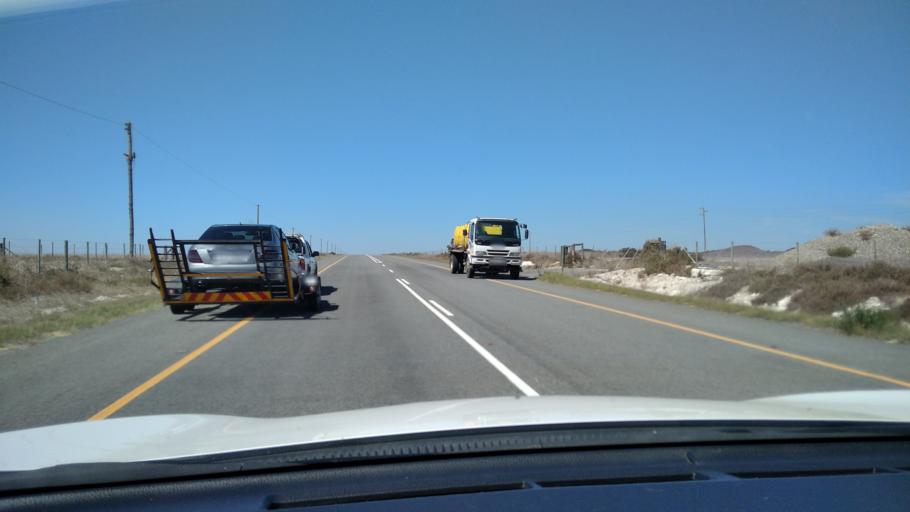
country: ZA
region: Western Cape
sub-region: West Coast District Municipality
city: Vredenburg
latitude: -32.9967
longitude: 18.1848
